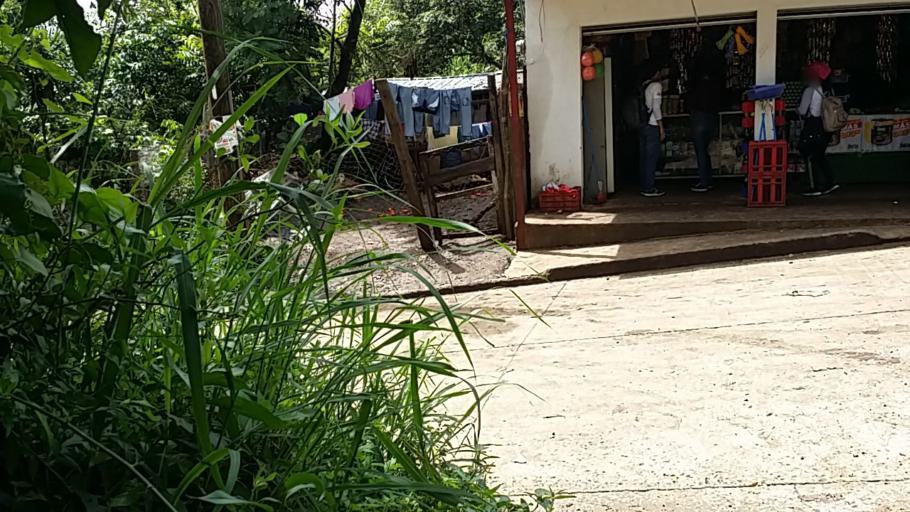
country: GT
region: Santa Rosa
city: Pueblo Nuevo Vinas
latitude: 14.3290
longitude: -90.5157
